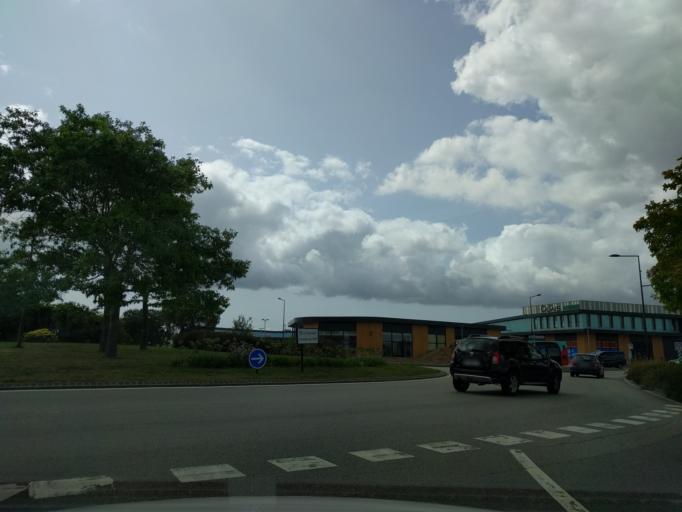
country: FR
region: Brittany
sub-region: Departement du Morbihan
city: Vannes
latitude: 47.6508
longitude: -2.7228
